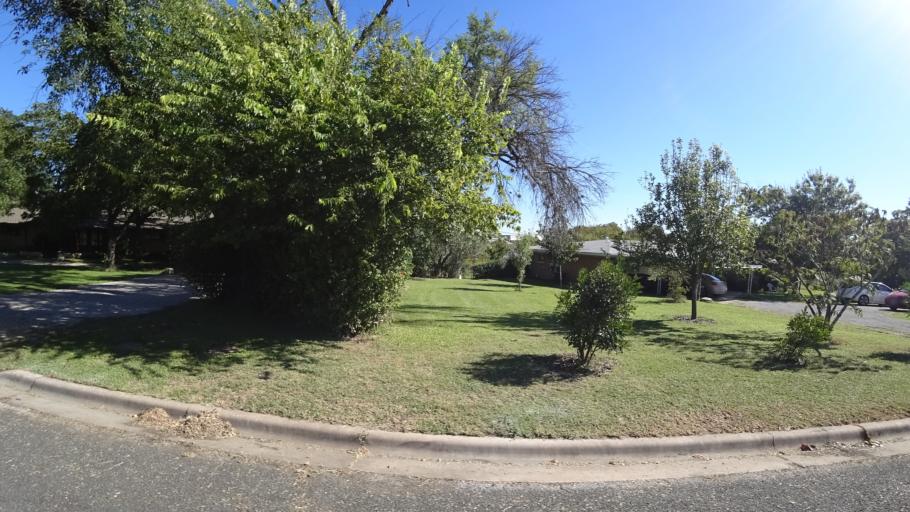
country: US
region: Texas
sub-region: Travis County
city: Austin
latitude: 30.2289
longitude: -97.7089
